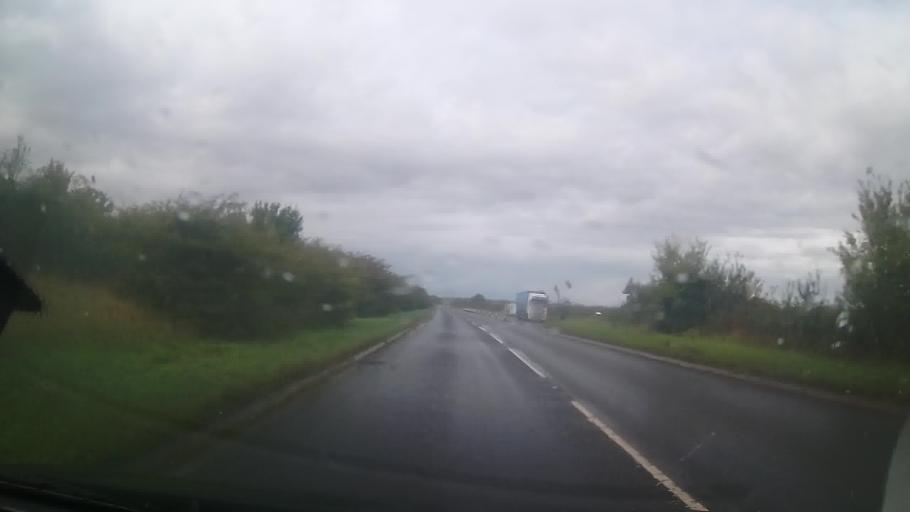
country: GB
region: England
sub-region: Worcestershire
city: Pershore
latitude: 52.1277
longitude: -2.0388
